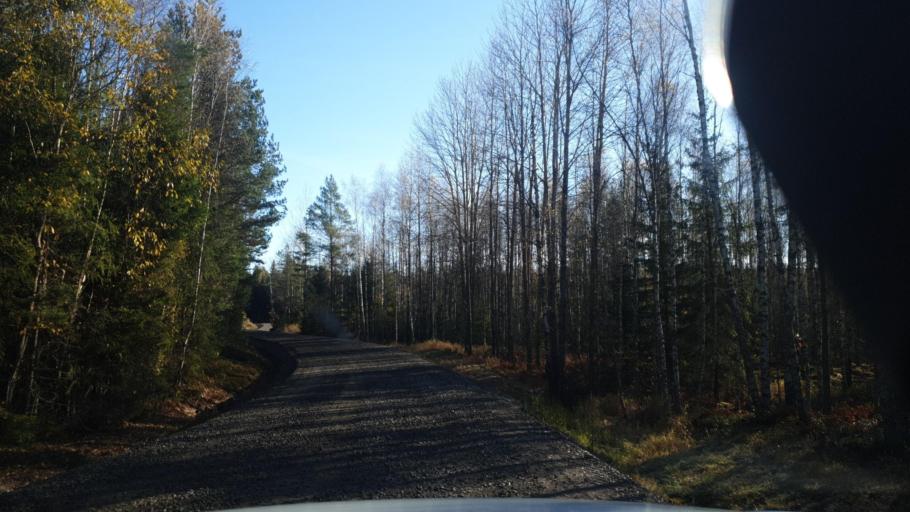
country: SE
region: Vaermland
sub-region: Karlstads Kommun
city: Valberg
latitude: 59.4161
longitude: 13.1278
